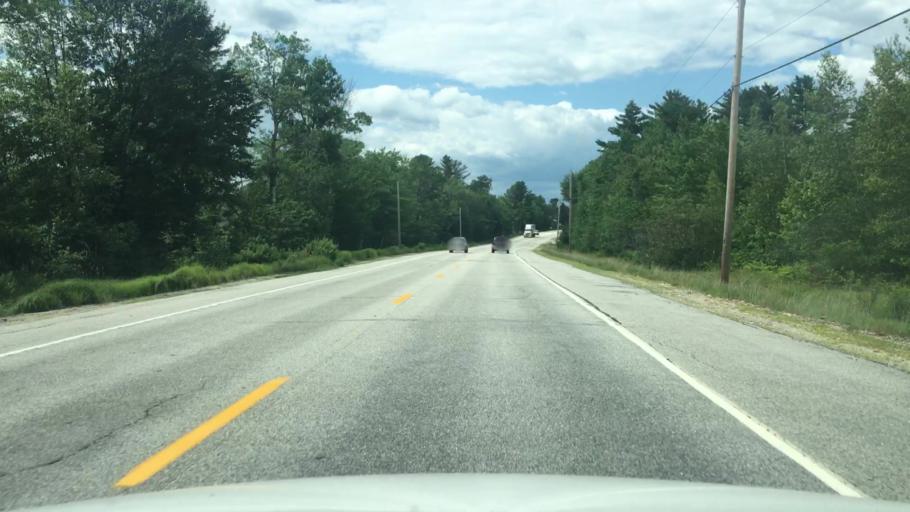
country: US
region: Maine
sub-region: Oxford County
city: West Paris
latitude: 44.3714
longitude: -70.6041
